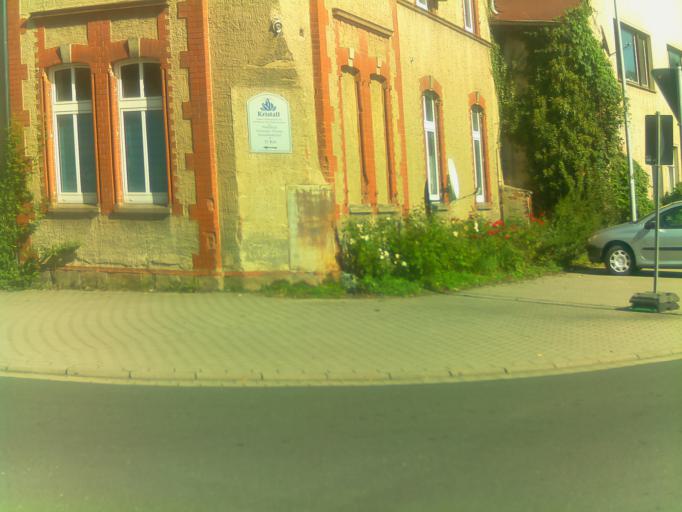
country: DE
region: Thuringia
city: Trobnitz
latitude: 50.8391
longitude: 11.7291
